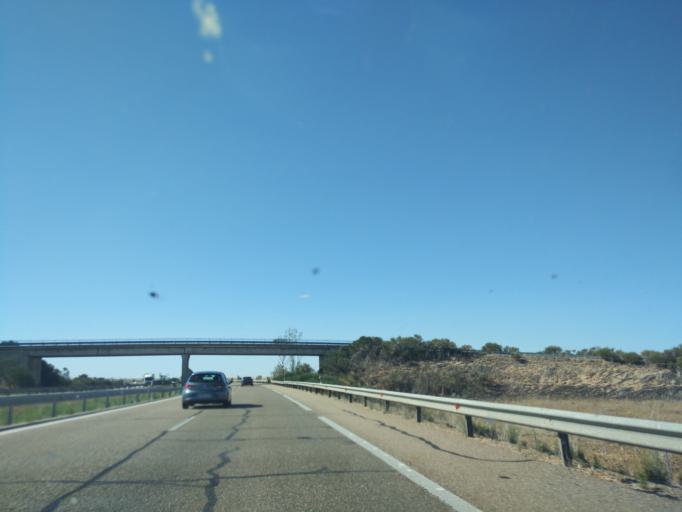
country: ES
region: Castille and Leon
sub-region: Provincia de Zamora
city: Villalpando
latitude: 41.8627
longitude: -5.4281
